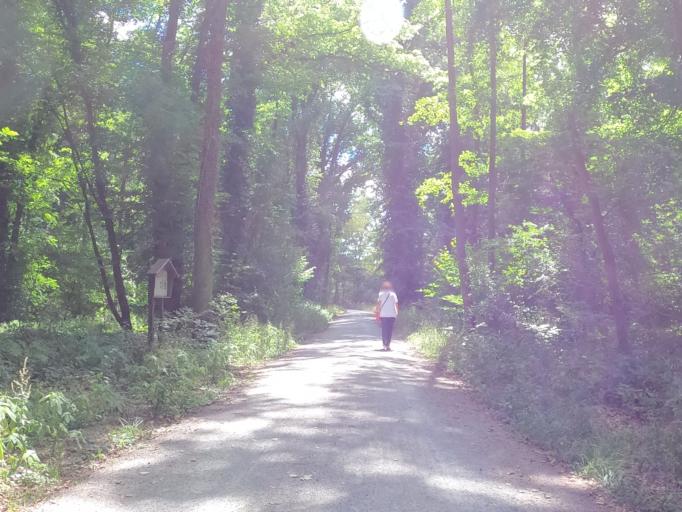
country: DE
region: Hesse
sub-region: Regierungsbezirk Darmstadt
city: Nauheim
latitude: 49.9645
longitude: 8.4637
